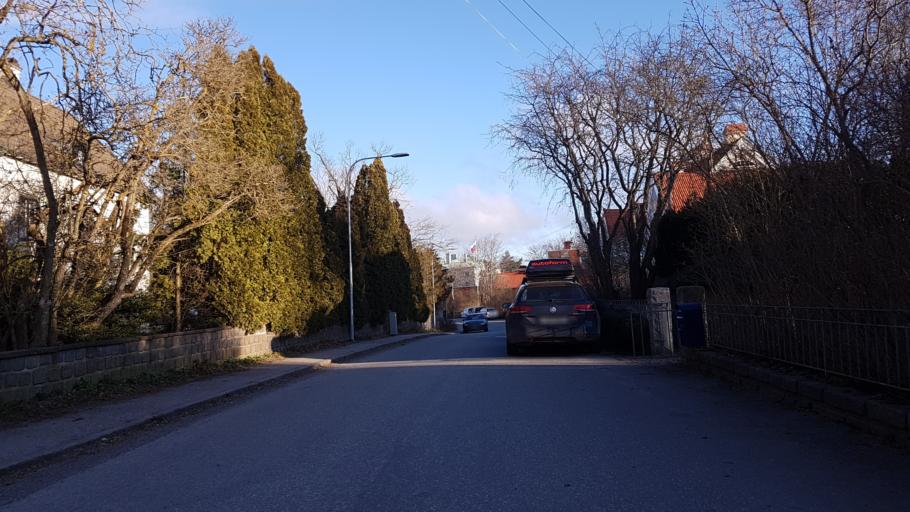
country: SE
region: Stockholm
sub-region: Lidingo
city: Lidingoe
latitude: 59.3606
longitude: 18.1254
